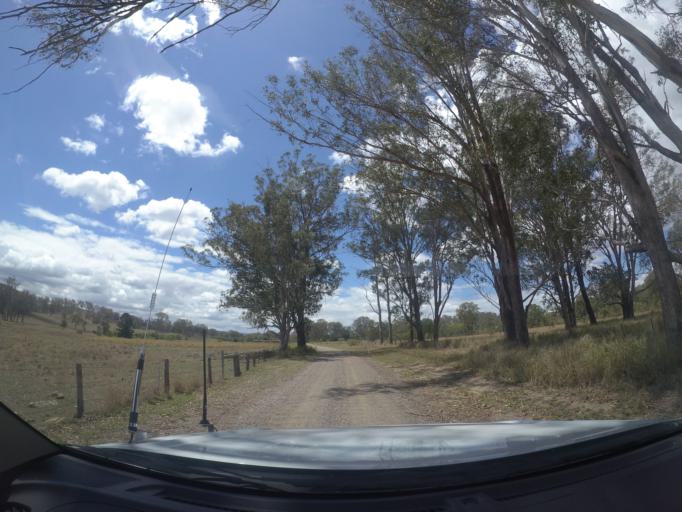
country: AU
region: Queensland
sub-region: Logan
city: Cedar Vale
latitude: -27.9020
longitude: 153.0608
